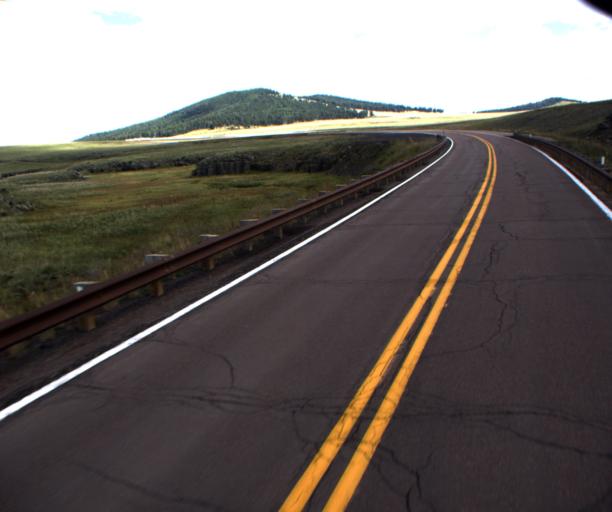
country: US
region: Arizona
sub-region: Apache County
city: Eagar
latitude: 34.0521
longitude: -109.5447
